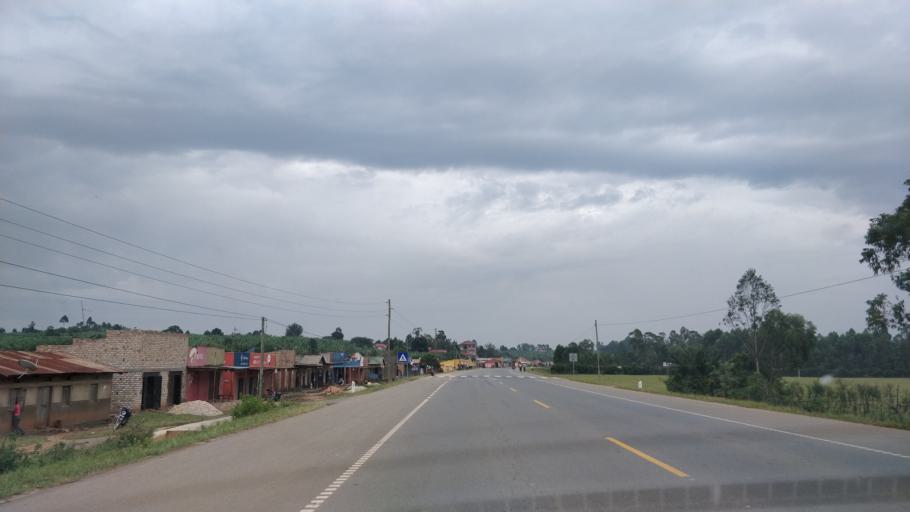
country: UG
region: Western Region
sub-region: Sheema District
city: Kibingo
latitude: -0.6618
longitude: 30.4540
